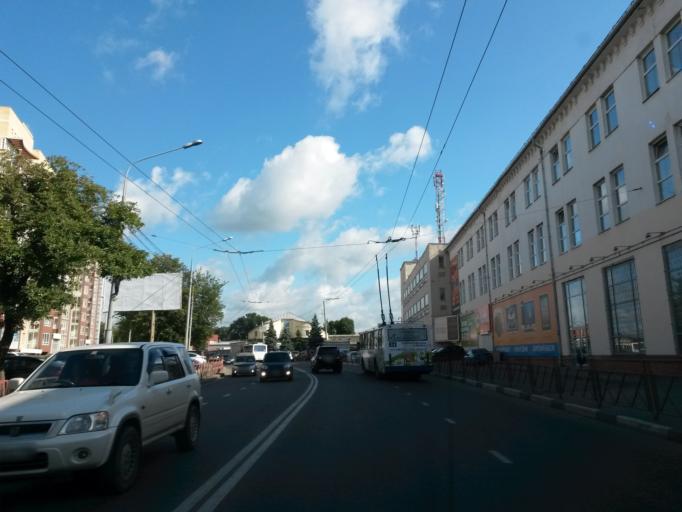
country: RU
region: Jaroslavl
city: Yaroslavl
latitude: 57.6404
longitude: 39.8835
